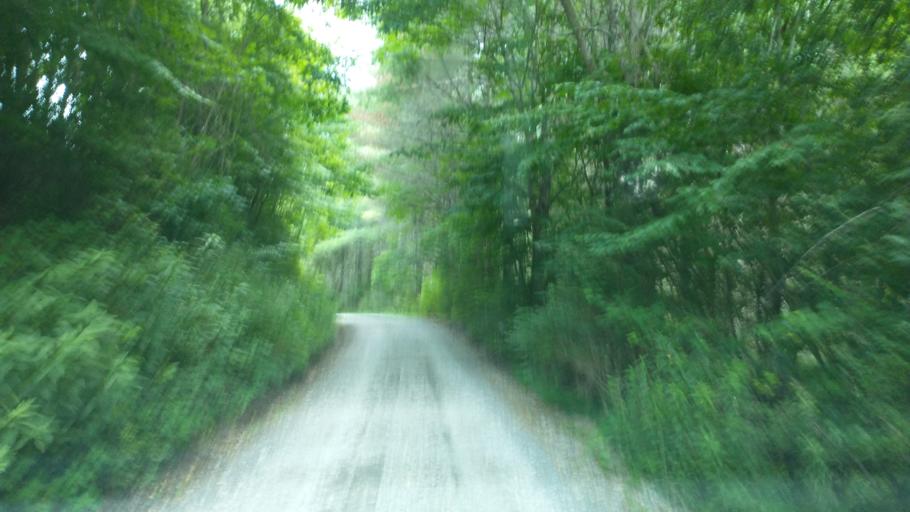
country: US
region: West Virginia
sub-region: Mercer County
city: Athens
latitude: 37.4369
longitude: -81.0037
